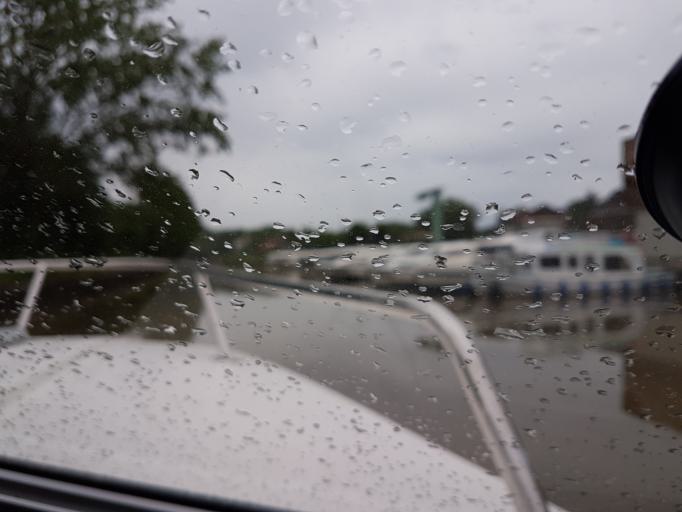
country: FR
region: Bourgogne
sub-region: Departement de la Nievre
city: Corbigny
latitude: 47.3617
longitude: 3.6192
